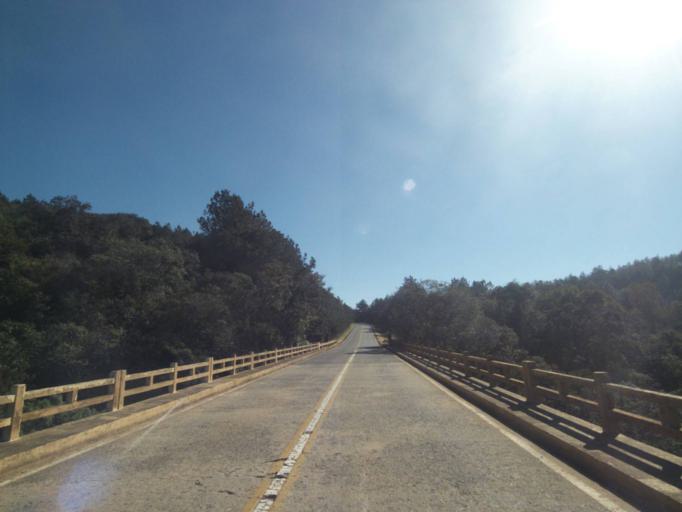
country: BR
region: Parana
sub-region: Telemaco Borba
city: Telemaco Borba
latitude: -24.4257
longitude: -50.5719
